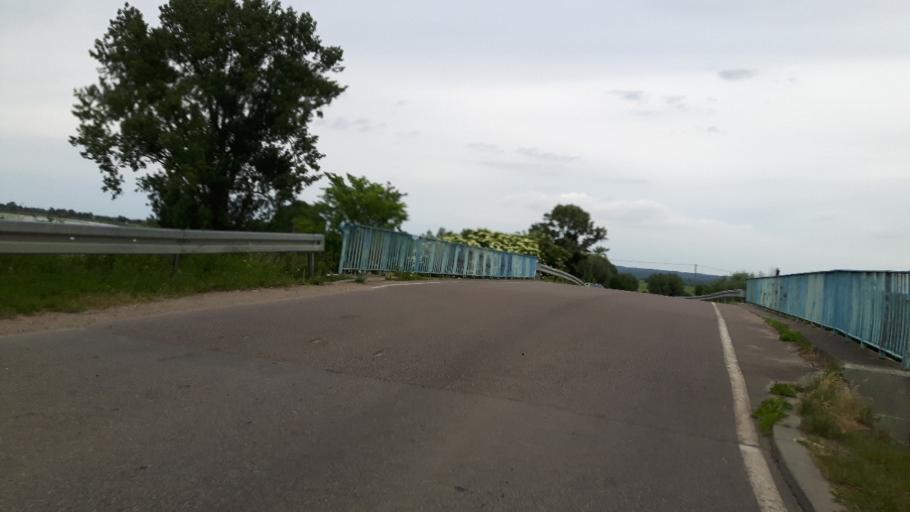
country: PL
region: Warmian-Masurian Voivodeship
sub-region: Powiat elblaski
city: Elblag
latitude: 54.1939
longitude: 19.3243
